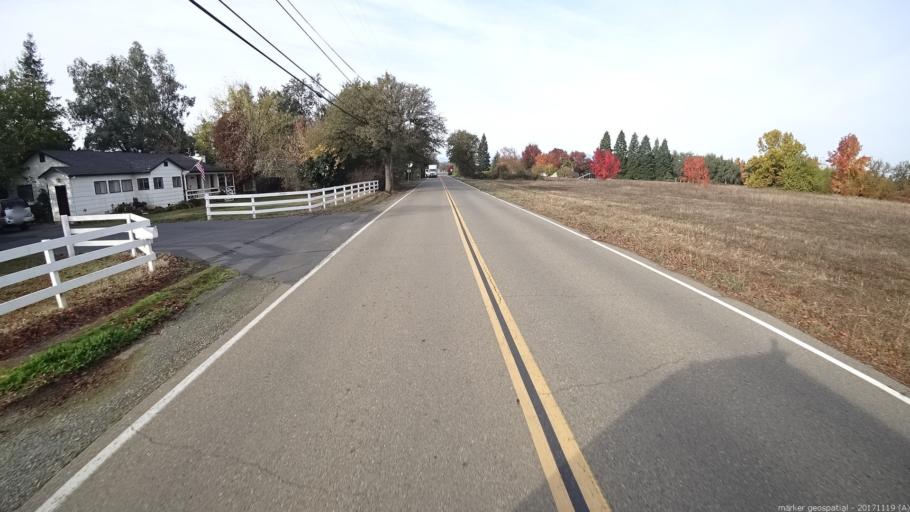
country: US
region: California
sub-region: Shasta County
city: Anderson
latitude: 40.5056
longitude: -122.3254
